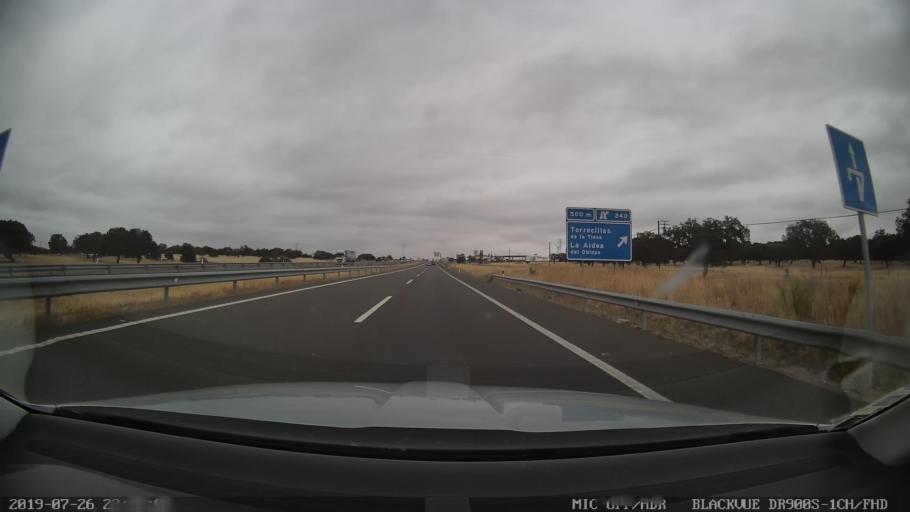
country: ES
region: Extremadura
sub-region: Provincia de Caceres
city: Torrecillas de la Tiesa
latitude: 39.5618
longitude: -5.8333
